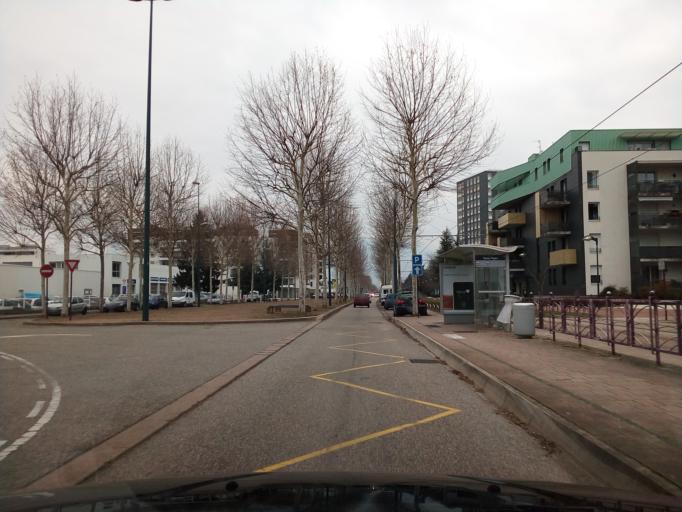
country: FR
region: Rhone-Alpes
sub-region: Departement de l'Isere
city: Le Pont-de-Claix
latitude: 45.1387
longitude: 5.7132
